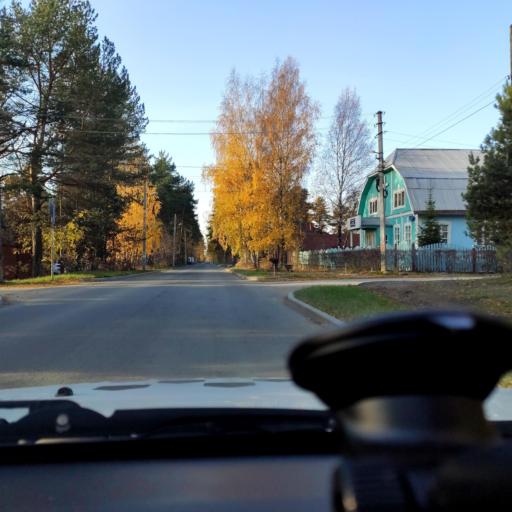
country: RU
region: Perm
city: Perm
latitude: 58.0528
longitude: 56.2941
